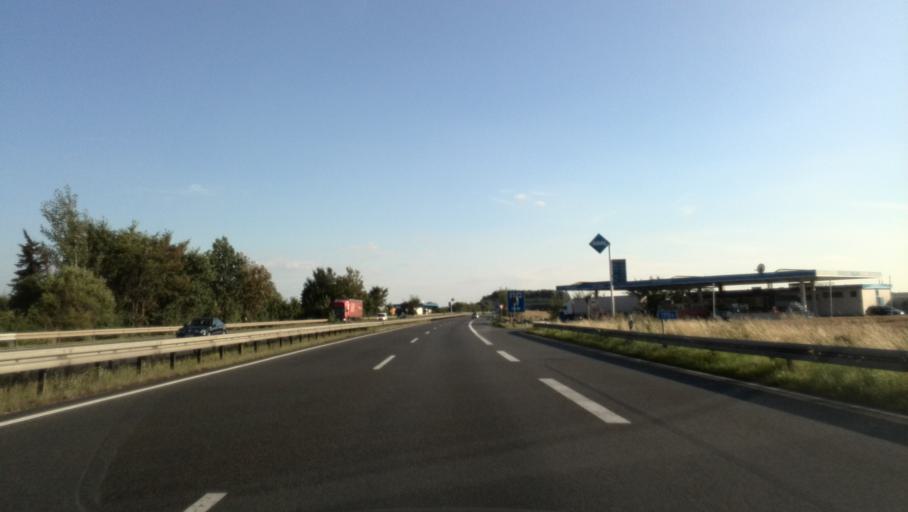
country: DE
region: Lower Saxony
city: Leiferde
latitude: 52.2152
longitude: 10.4946
